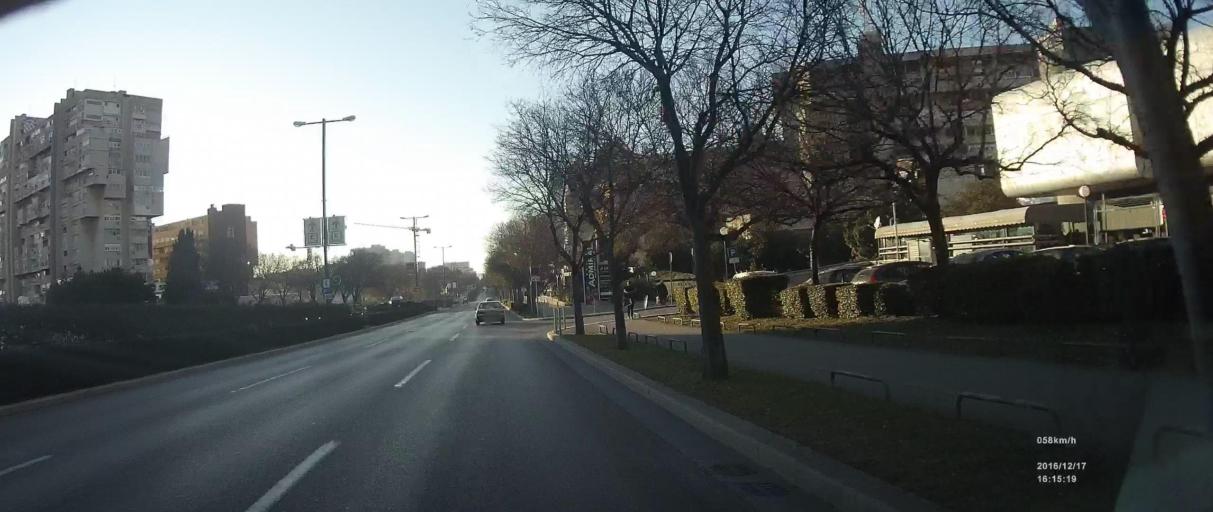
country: HR
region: Splitsko-Dalmatinska
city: Vranjic
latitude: 43.5073
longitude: 16.4677
